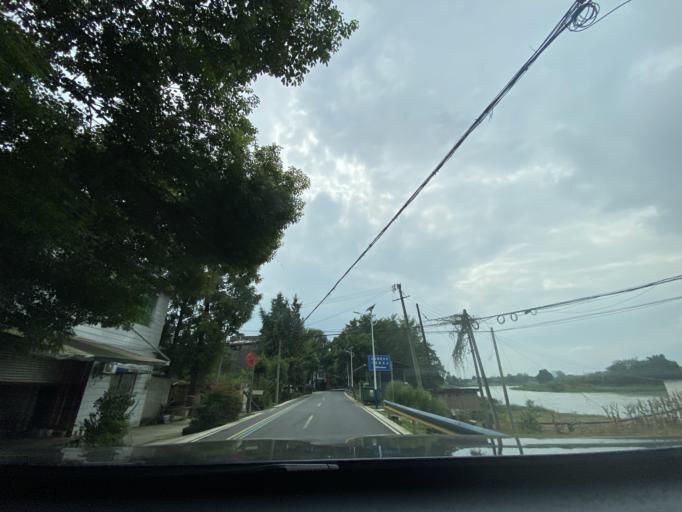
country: CN
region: Sichuan
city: Wujin
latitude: 30.3978
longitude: 103.9867
